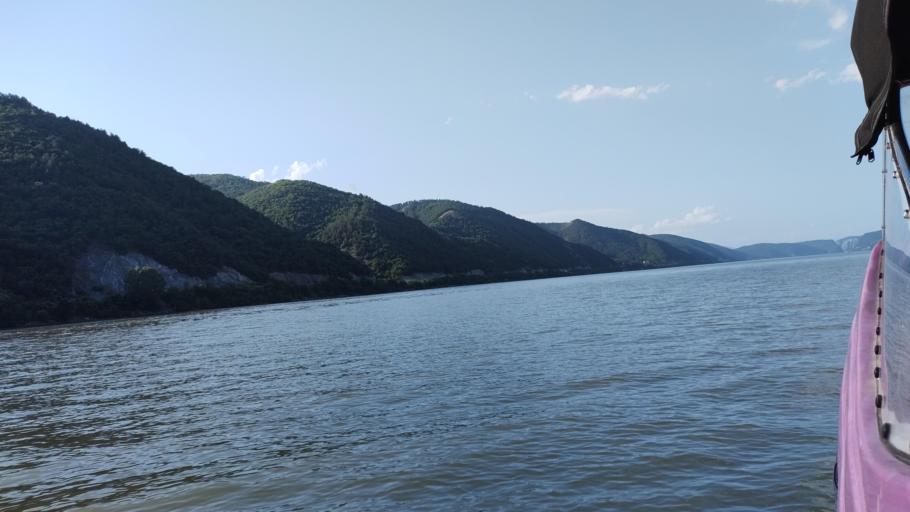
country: RO
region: Mehedinti
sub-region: Comuna Svinita
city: Svinita
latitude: 44.4948
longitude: 22.1884
